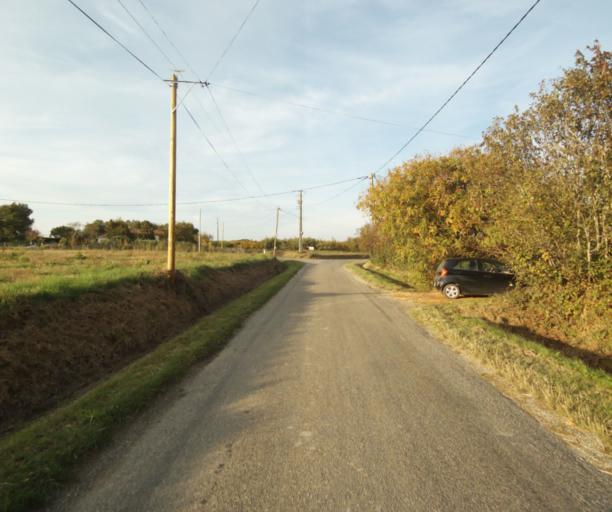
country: FR
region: Midi-Pyrenees
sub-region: Departement du Tarn-et-Garonne
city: Campsas
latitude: 43.8777
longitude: 1.3492
